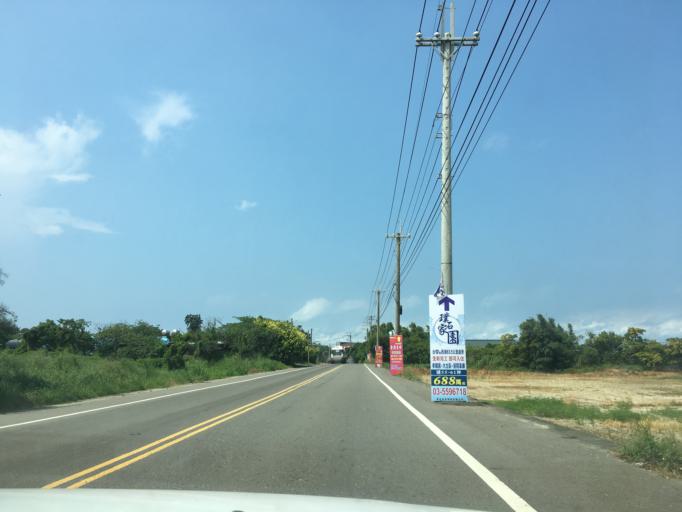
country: TW
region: Taiwan
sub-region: Hsinchu
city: Zhubei
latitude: 24.8953
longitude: 120.9685
